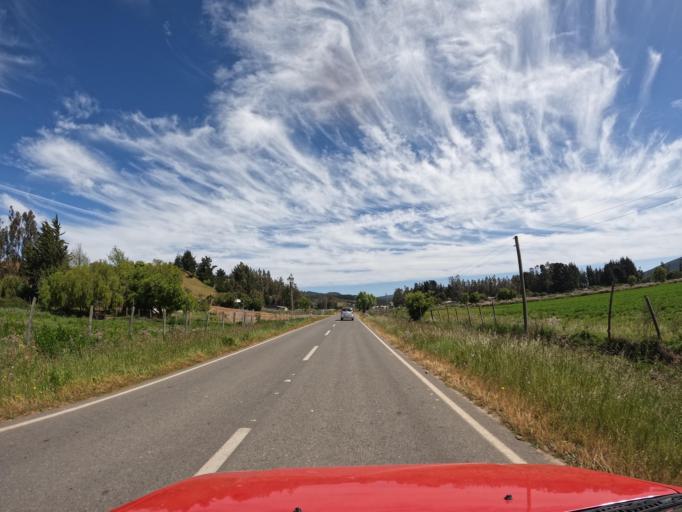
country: CL
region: Maule
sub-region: Provincia de Talca
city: Constitucion
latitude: -35.0133
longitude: -72.0371
